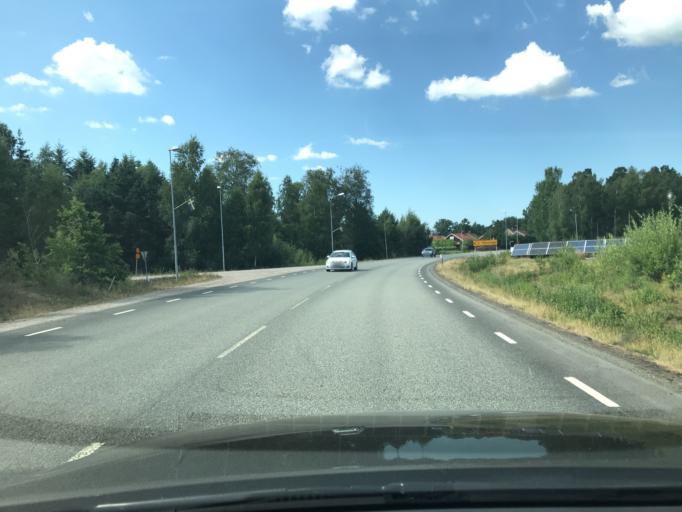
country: SE
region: Skane
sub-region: Hassleholms Kommun
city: Hastveda
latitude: 56.2793
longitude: 13.9333
